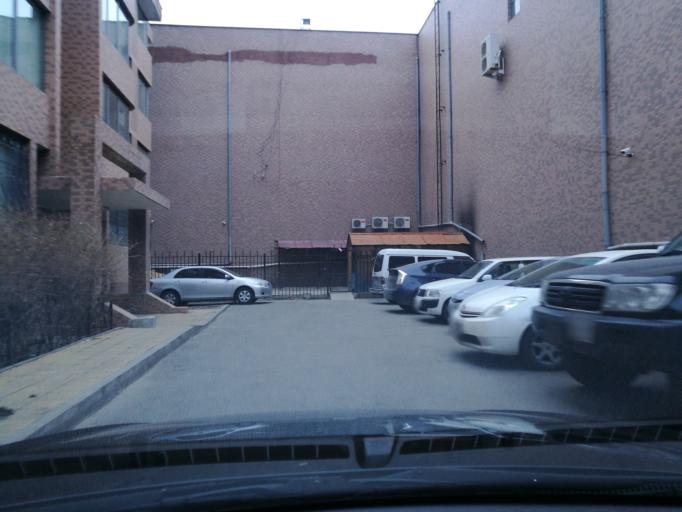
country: MN
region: Ulaanbaatar
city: Ulaanbaatar
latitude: 47.9267
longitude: 106.9151
